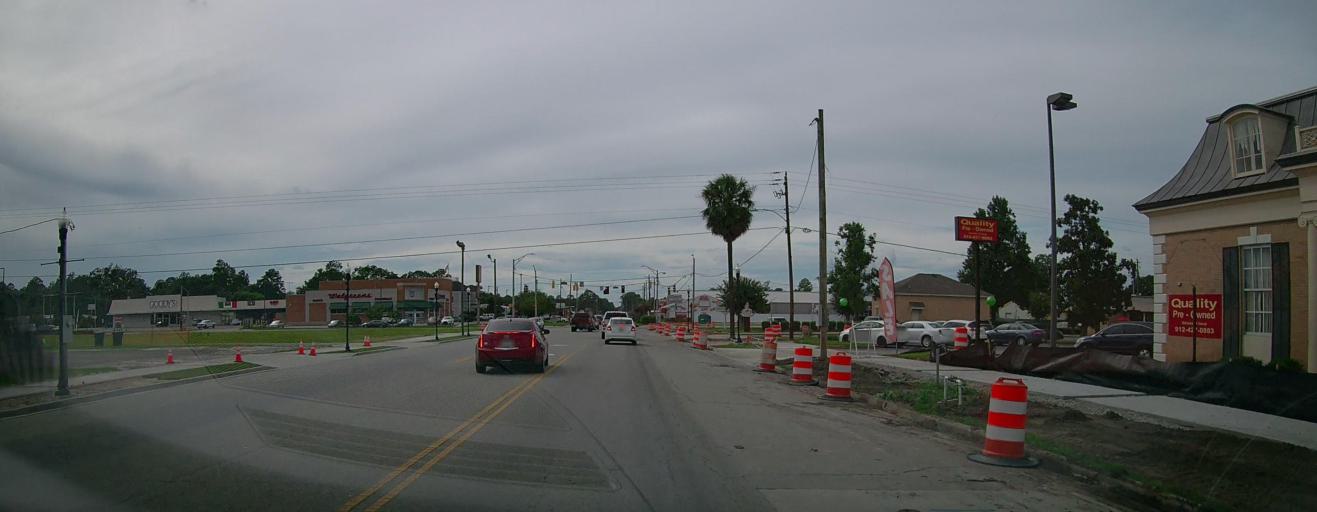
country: US
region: Georgia
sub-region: Wayne County
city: Jesup
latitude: 31.6064
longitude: -81.8843
